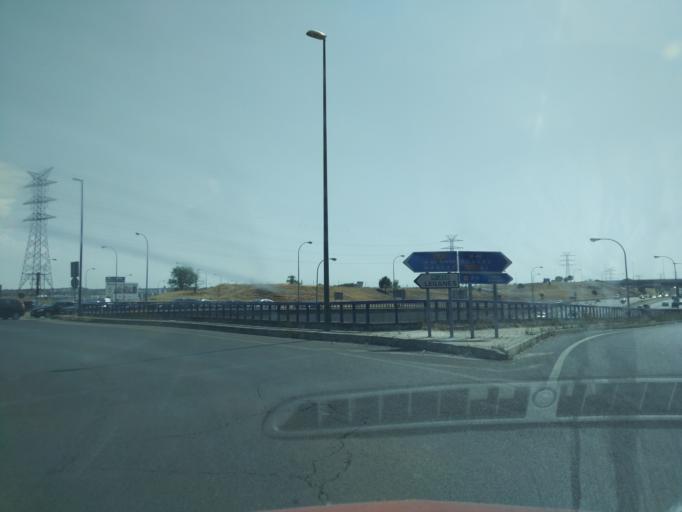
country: ES
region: Madrid
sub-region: Provincia de Madrid
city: Latina
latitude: 40.3621
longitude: -3.7451
